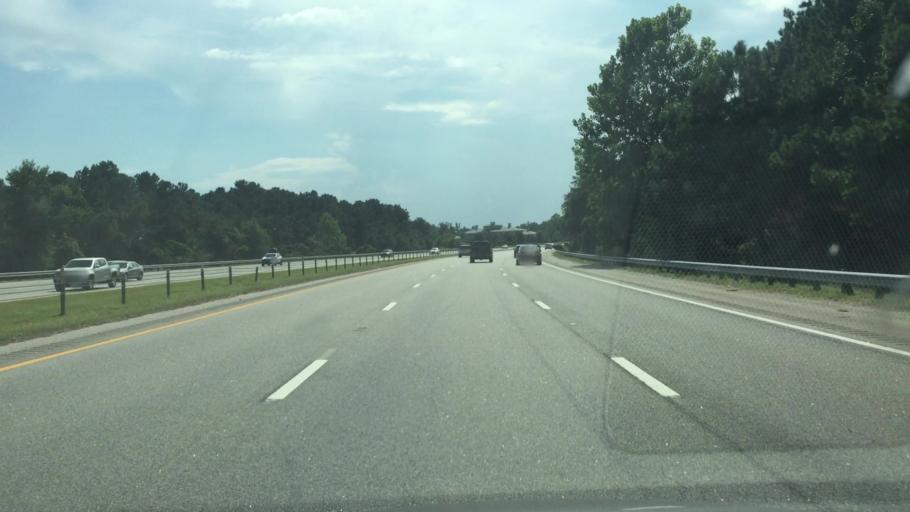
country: US
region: South Carolina
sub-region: Horry County
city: North Myrtle Beach
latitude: 33.8161
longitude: -78.7426
